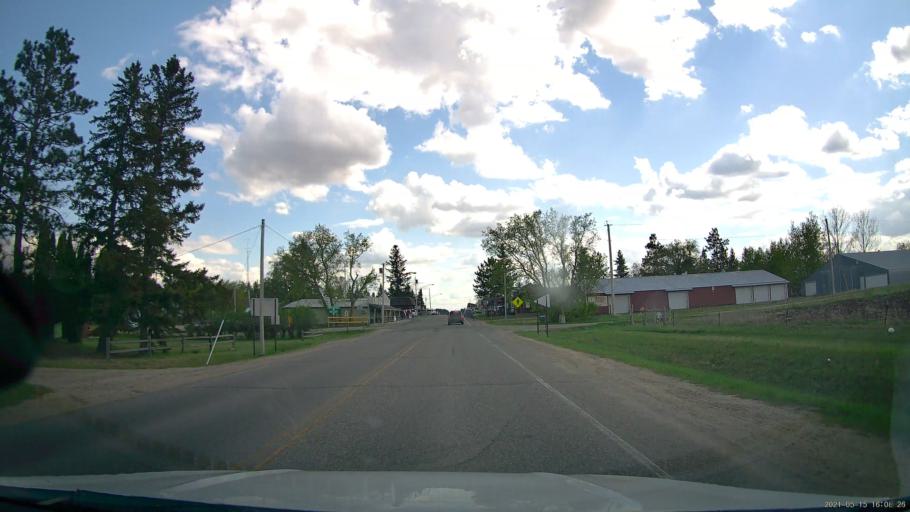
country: US
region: Minnesota
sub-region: Hubbard County
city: Park Rapids
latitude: 46.9581
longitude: -94.9527
